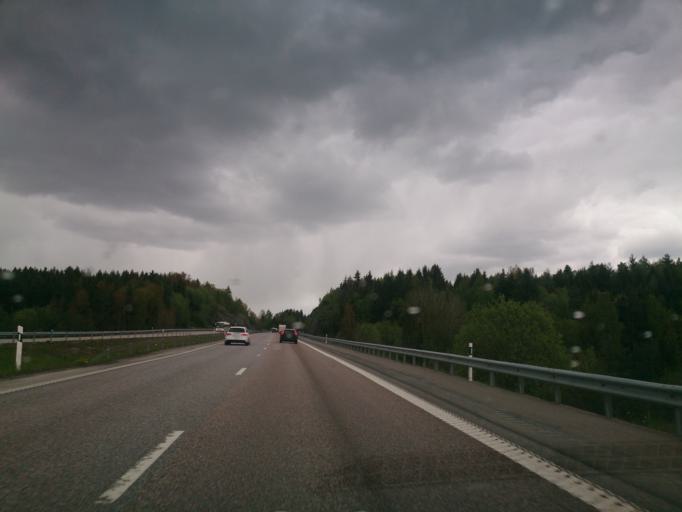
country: SE
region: Soedermanland
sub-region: Trosa Kommun
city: Vagnharad
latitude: 58.9946
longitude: 17.5363
